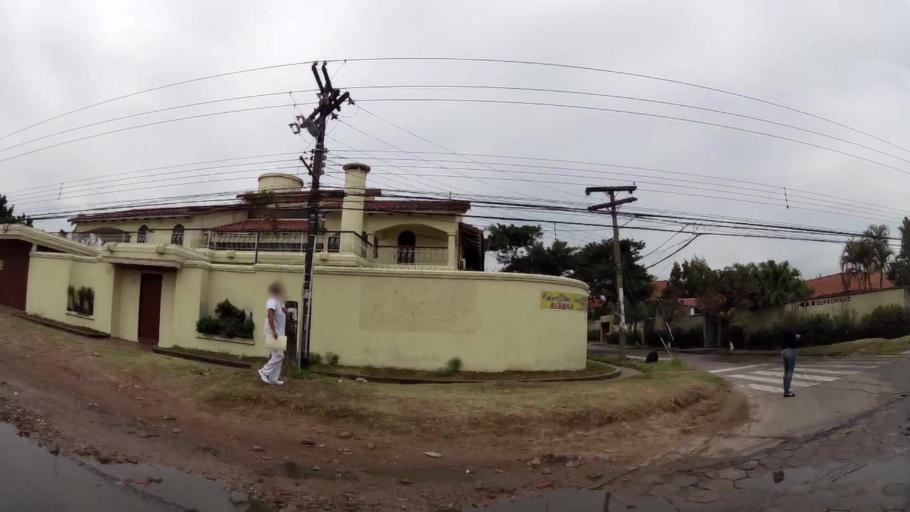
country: BO
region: Santa Cruz
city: Santa Cruz de la Sierra
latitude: -17.7615
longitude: -63.1659
